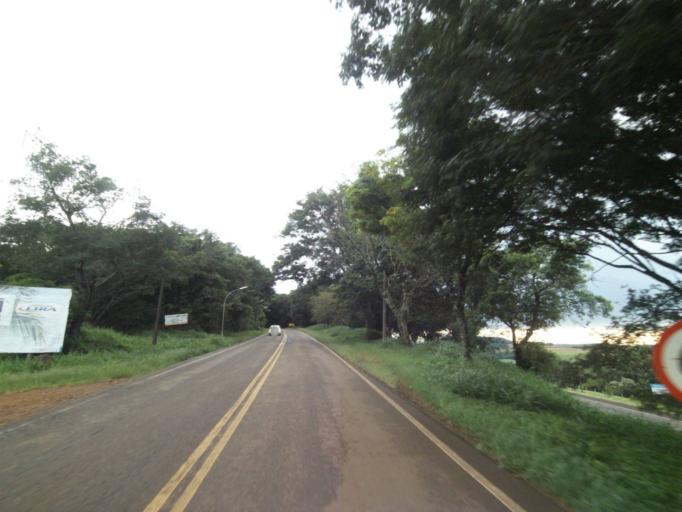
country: BR
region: Parana
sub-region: Guaraniacu
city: Guaraniacu
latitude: -25.0999
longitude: -52.8936
